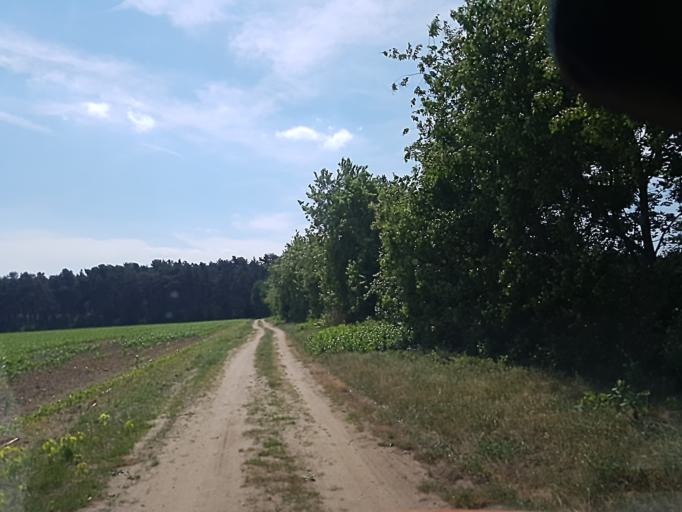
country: DE
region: Brandenburg
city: Gorzke
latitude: 52.1270
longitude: 12.3125
